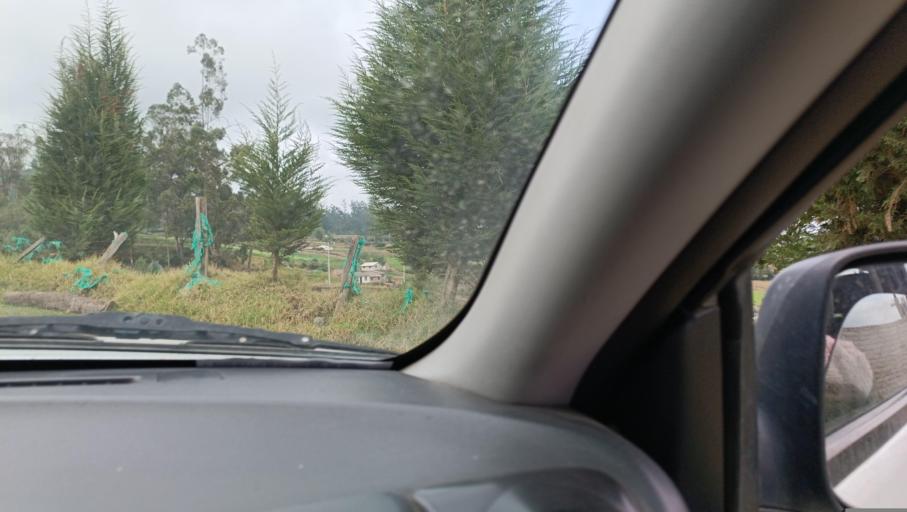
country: EC
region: Chimborazo
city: Riobamba
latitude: -1.6591
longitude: -78.5659
